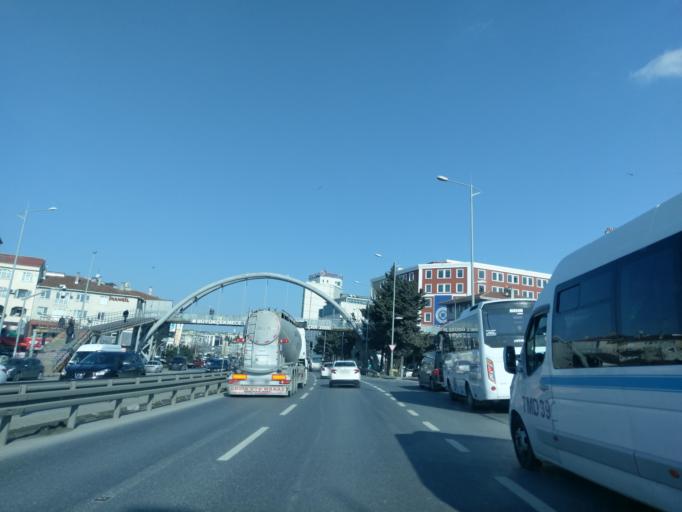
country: TR
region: Istanbul
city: Bueyuekcekmece
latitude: 41.0203
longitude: 28.5809
